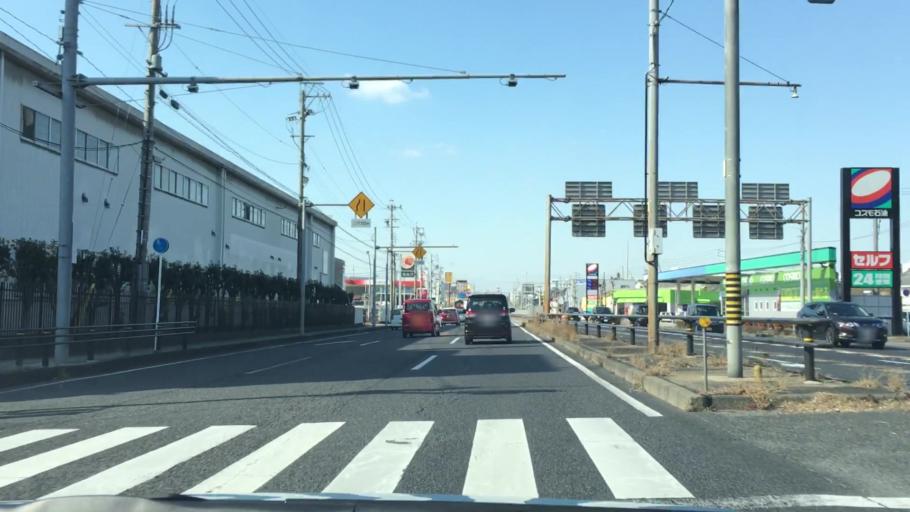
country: JP
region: Aichi
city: Okazaki
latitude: 34.9471
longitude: 137.1871
